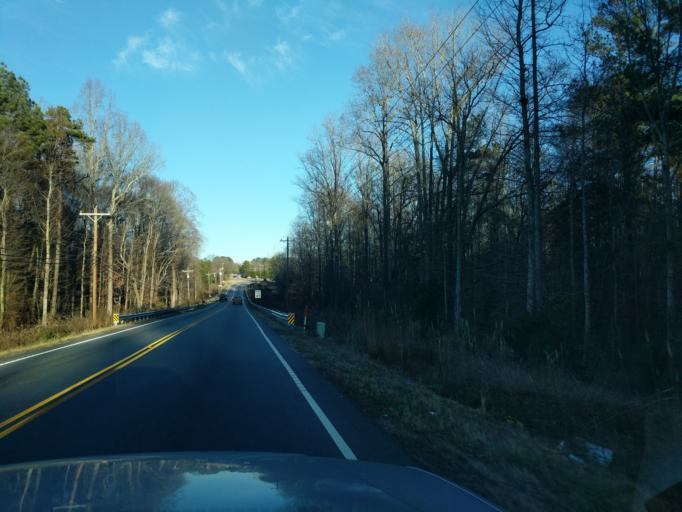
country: US
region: South Carolina
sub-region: Greenville County
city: Fountain Inn
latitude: 34.6722
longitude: -82.2355
